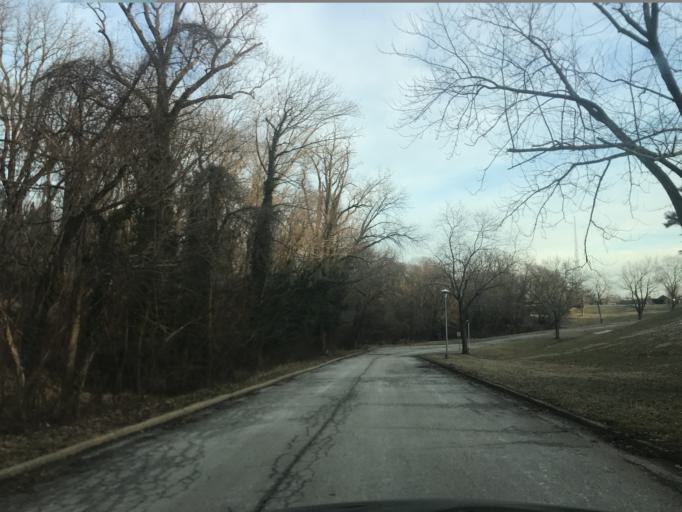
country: US
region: Maryland
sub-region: Baltimore County
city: Charlestown
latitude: 39.2665
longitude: -76.7180
